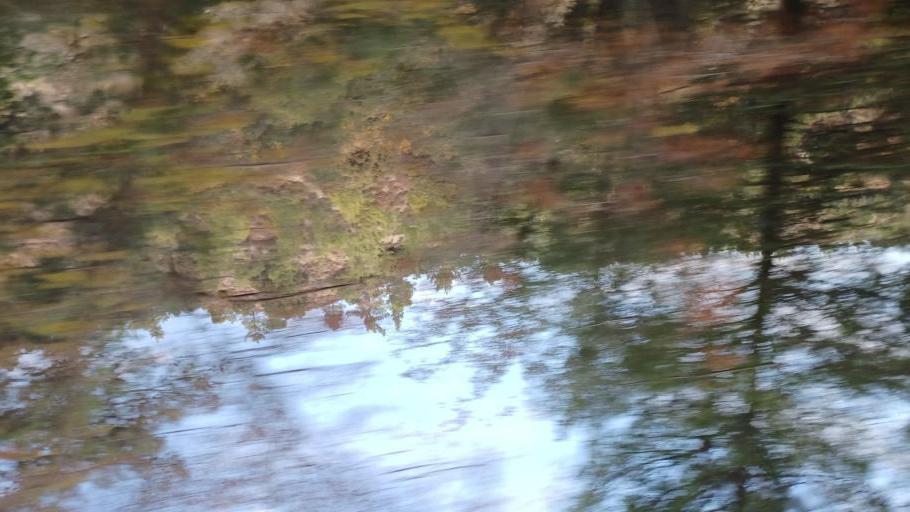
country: CY
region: Lefkosia
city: Kakopetria
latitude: 34.9740
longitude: 32.9133
